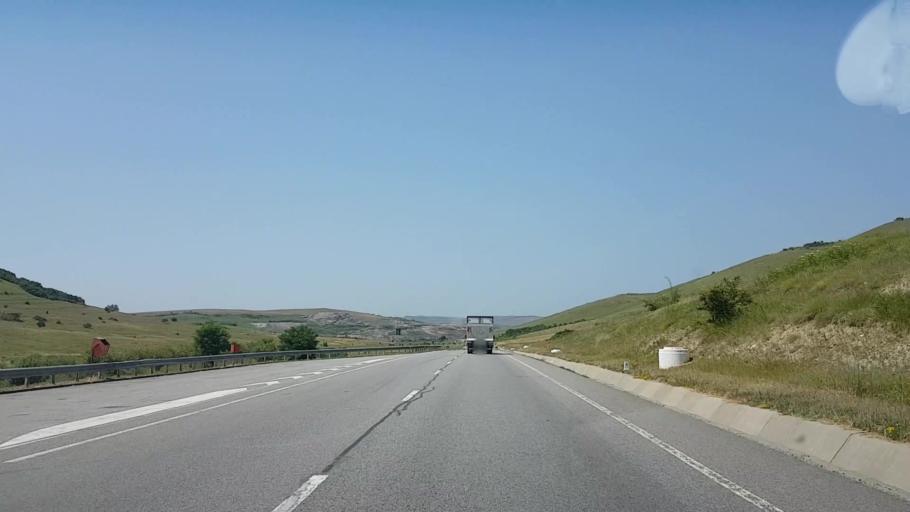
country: RO
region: Cluj
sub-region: Comuna Apahida
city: Dezmir
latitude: 46.7509
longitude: 23.7045
